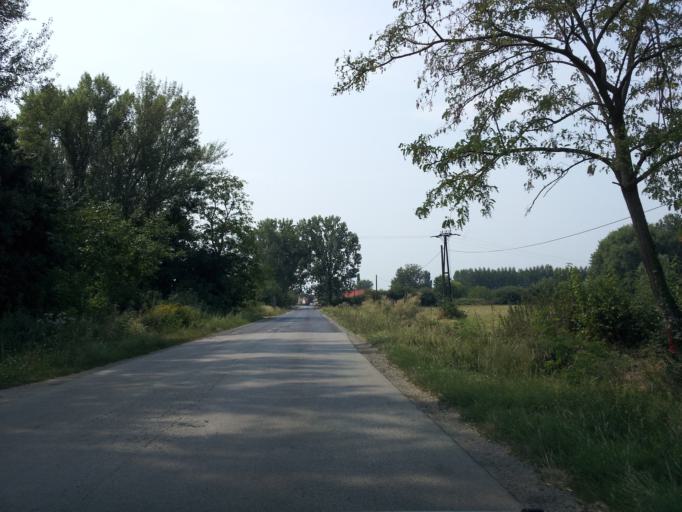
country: HU
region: Gyor-Moson-Sopron
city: Farad
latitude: 47.5881
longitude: 17.1925
